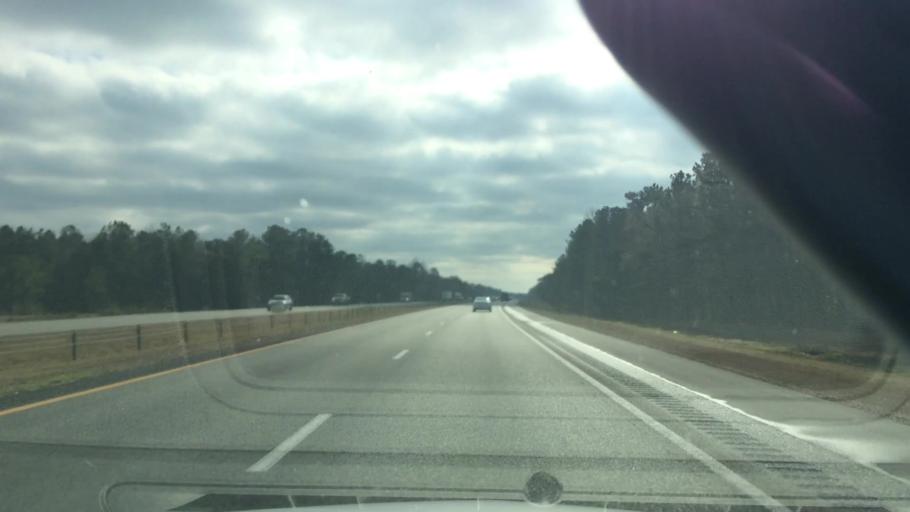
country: US
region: North Carolina
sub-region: Pender County
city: Rocky Point
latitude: 34.4151
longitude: -77.8696
